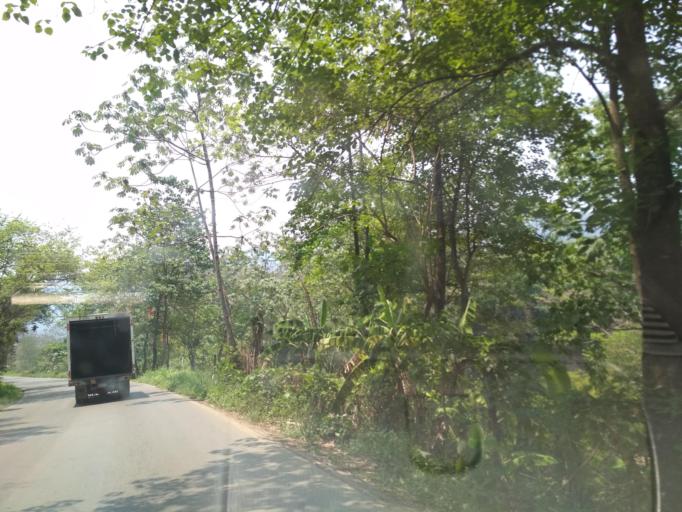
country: MX
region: Veracruz
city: Tezonapa
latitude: 18.6057
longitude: -96.6913
